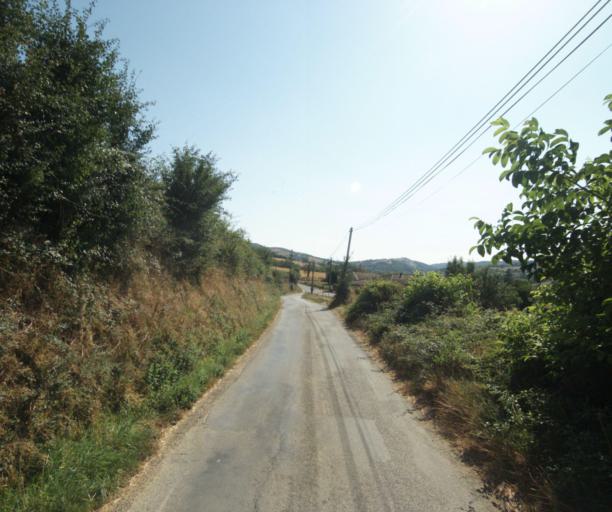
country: FR
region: Rhone-Alpes
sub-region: Departement du Rhone
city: Courzieu
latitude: 45.7577
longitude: 4.5636
